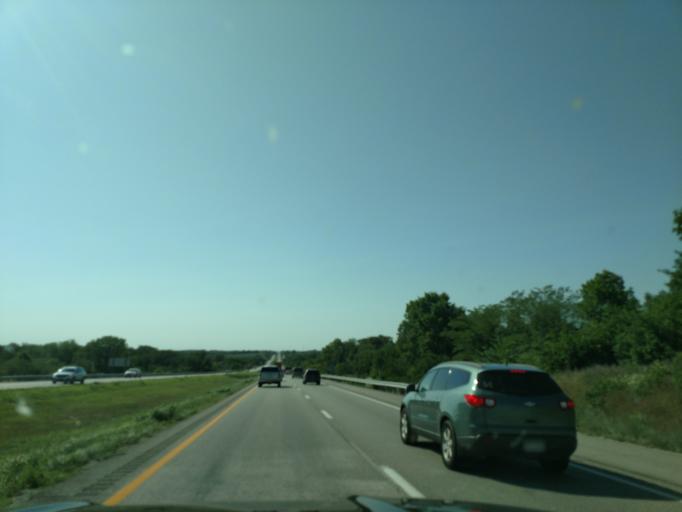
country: US
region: Missouri
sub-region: Andrew County
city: Country Club Village
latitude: 39.8618
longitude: -94.8165
